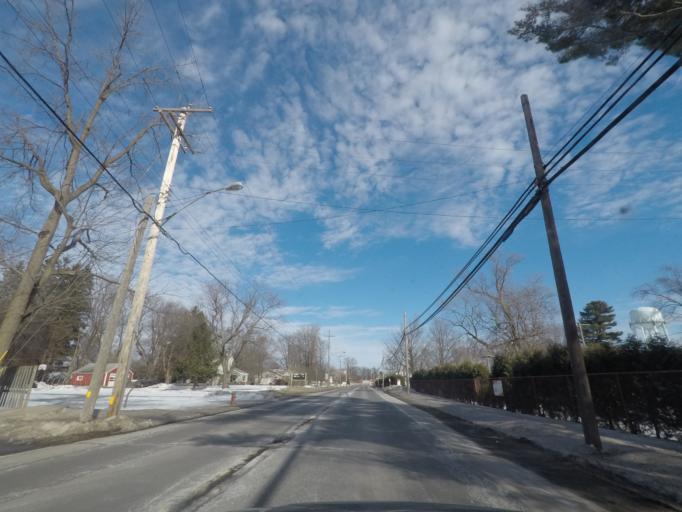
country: US
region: New York
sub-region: Schenectady County
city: Rotterdam
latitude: 42.7894
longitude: -73.9850
